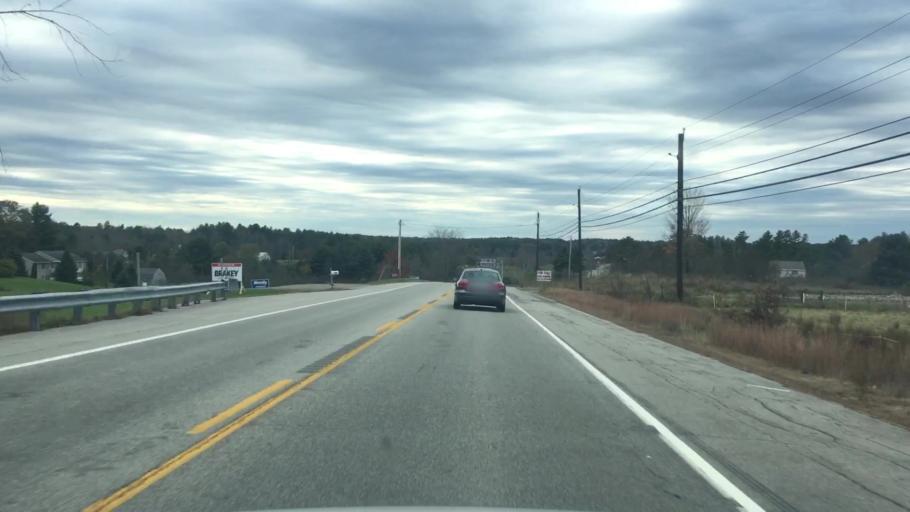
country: US
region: Maine
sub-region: York County
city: West Kennebunk
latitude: 43.4746
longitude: -70.5433
